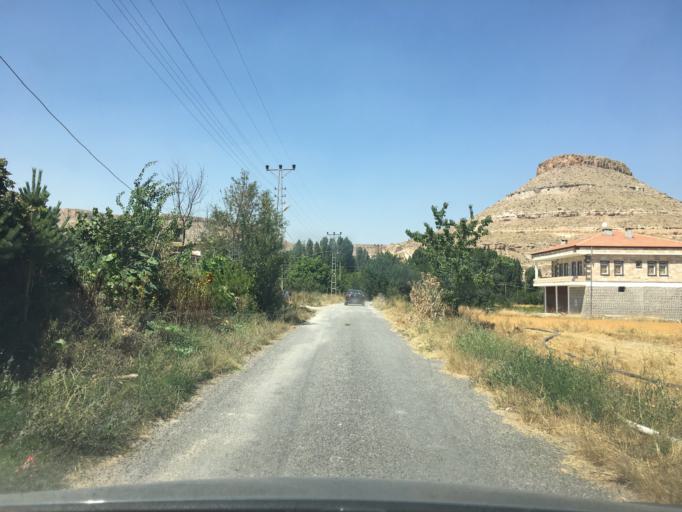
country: TR
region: Nevsehir
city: Urgub
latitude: 38.4682
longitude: 34.9622
